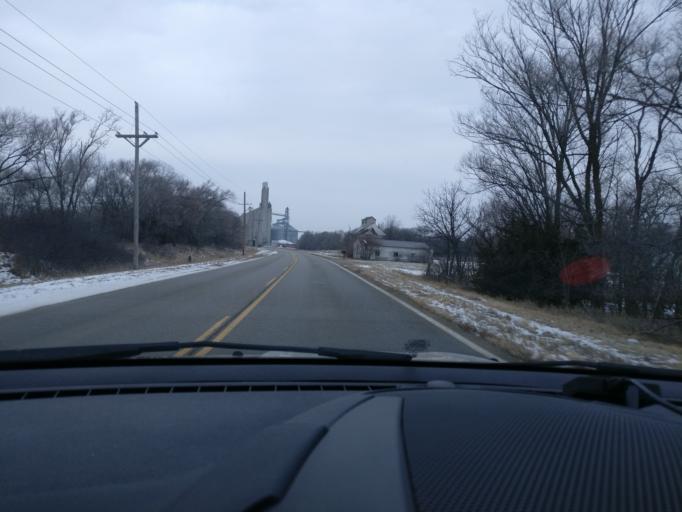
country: US
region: Nebraska
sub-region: Dodge County
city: Fremont
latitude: 41.4464
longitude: -96.5473
